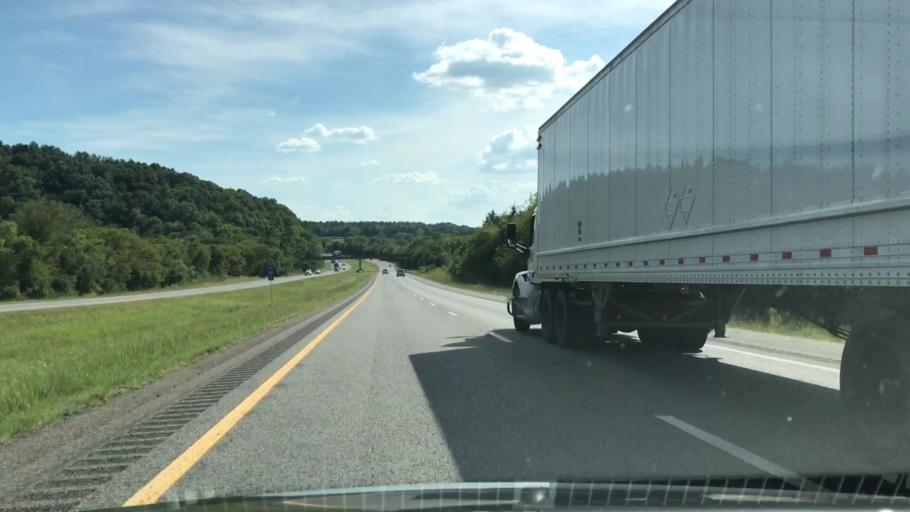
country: US
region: Alabama
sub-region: Limestone County
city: Ardmore
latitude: 35.1114
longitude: -86.8828
